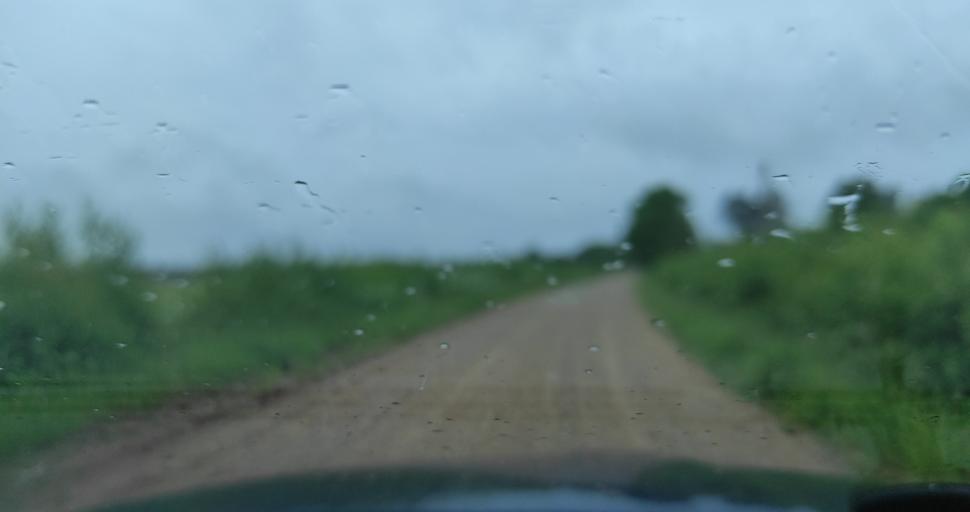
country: LV
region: Alsunga
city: Alsunga
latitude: 56.9800
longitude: 21.3679
